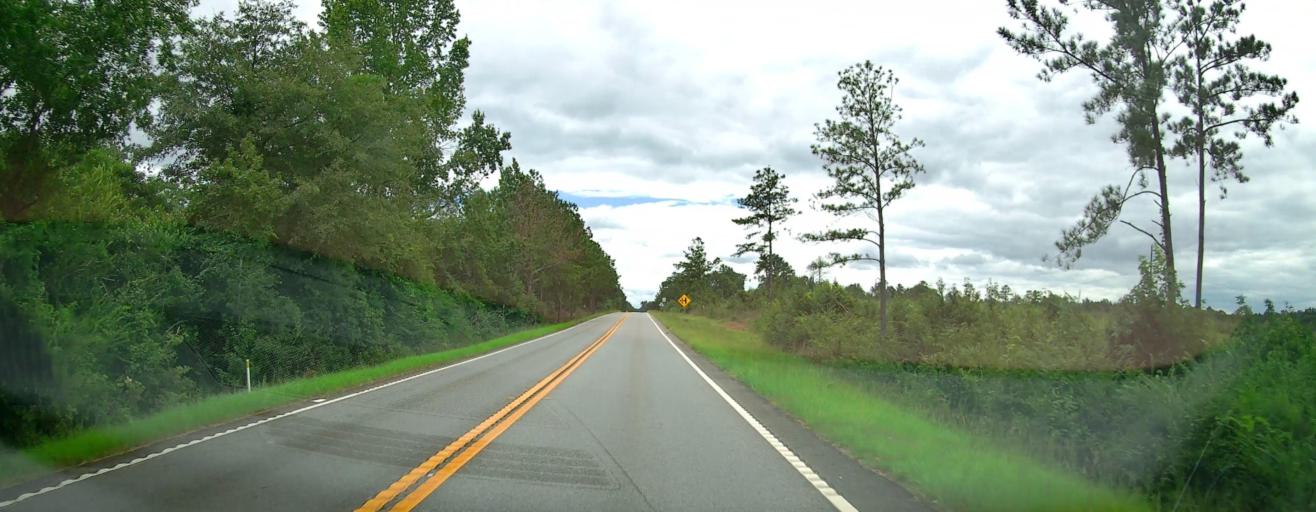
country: US
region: Georgia
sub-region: Twiggs County
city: Jeffersonville
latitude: 32.6699
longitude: -83.3272
